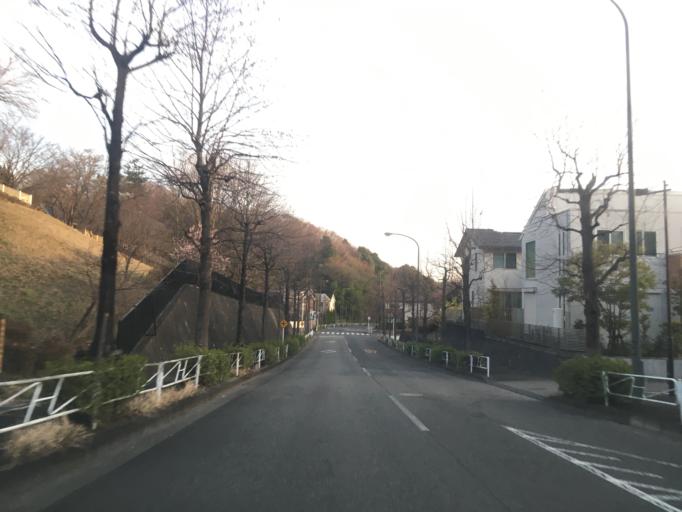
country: JP
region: Tokyo
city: Hachioji
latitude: 35.6104
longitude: 139.3570
